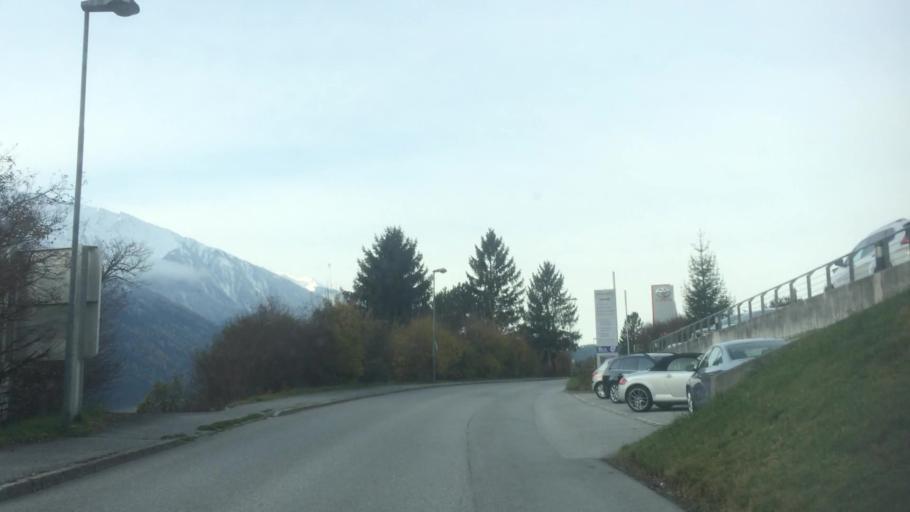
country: AT
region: Tyrol
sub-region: Politischer Bezirk Innsbruck Land
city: Pfaffenhofen
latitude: 47.3158
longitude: 11.0900
